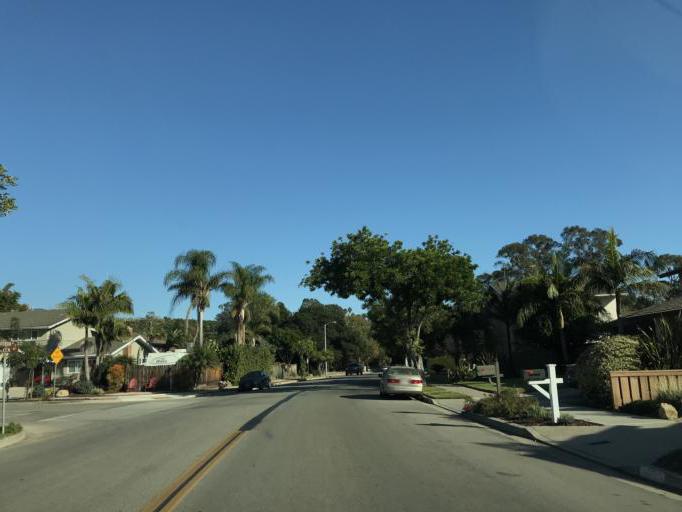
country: US
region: California
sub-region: Santa Barbara County
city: Goleta
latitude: 34.4580
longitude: -119.8117
